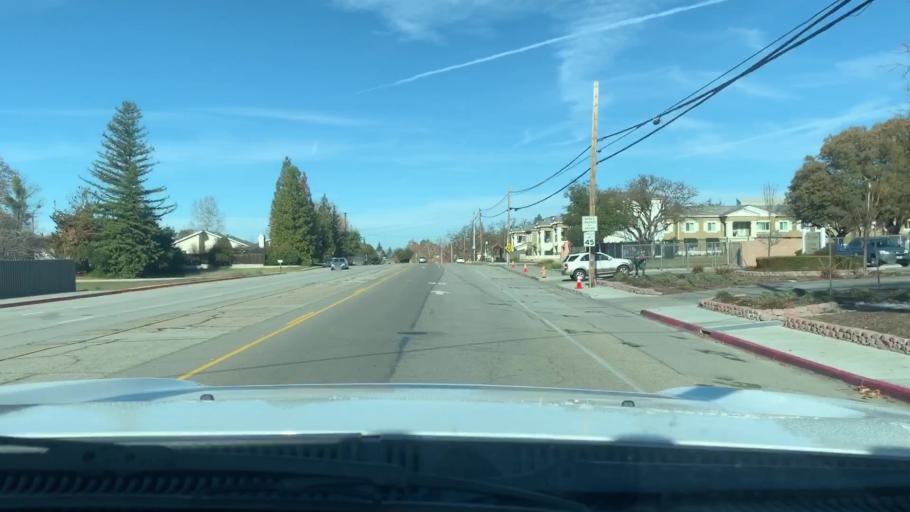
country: US
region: California
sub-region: San Luis Obispo County
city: Atascadero
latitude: 35.4565
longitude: -120.6407
